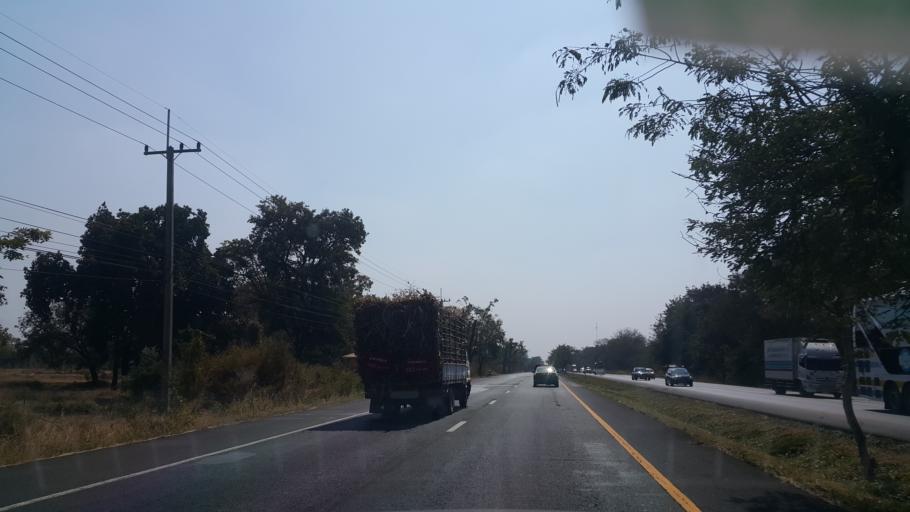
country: TH
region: Nakhon Ratchasima
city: Non Daeng
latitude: 15.3712
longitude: 102.4577
